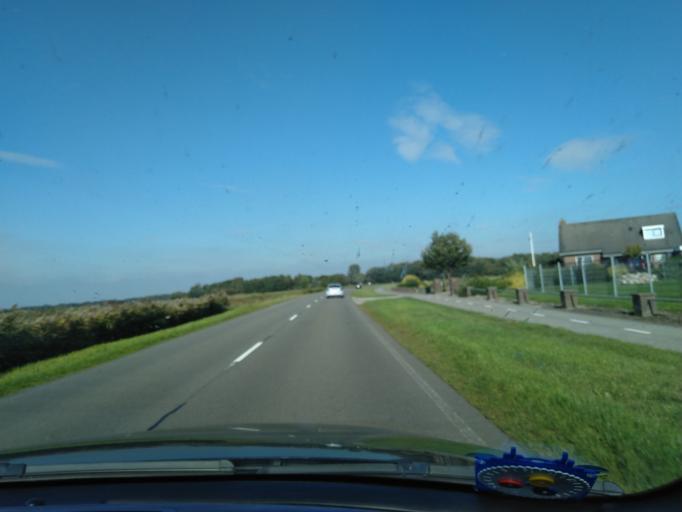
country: NL
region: Drenthe
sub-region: Gemeente Aa en Hunze
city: Anloo
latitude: 53.0700
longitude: 6.7603
